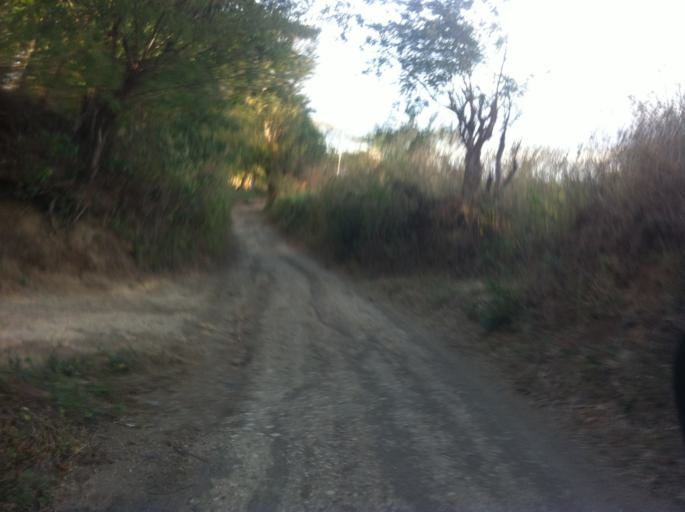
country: NI
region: Managua
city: El Crucero
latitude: 12.0709
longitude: -86.3092
